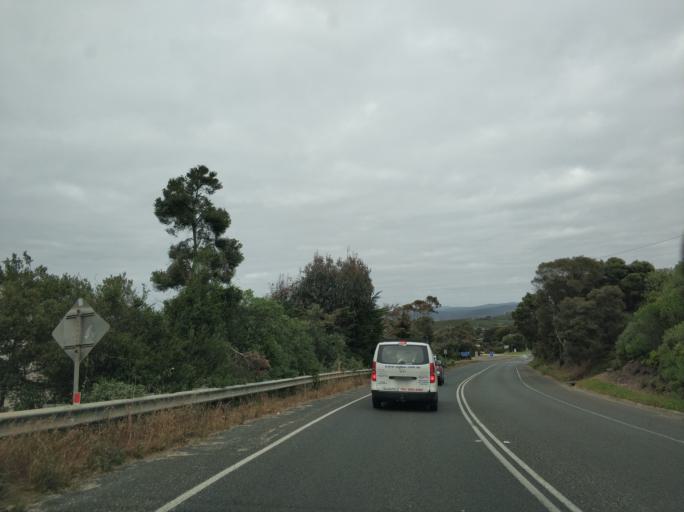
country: AU
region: Victoria
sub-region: Surf Coast
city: Anglesea
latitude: -38.4638
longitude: 144.1038
